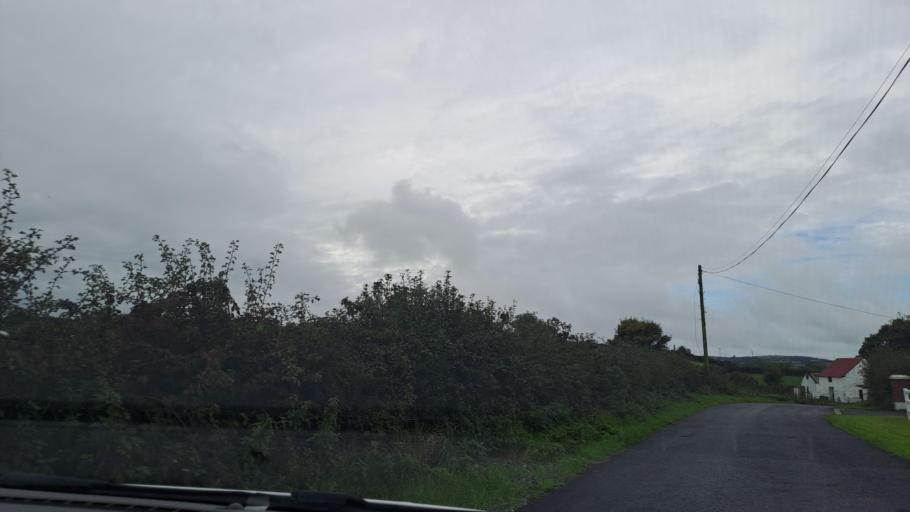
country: IE
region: Ulster
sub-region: An Cabhan
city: Kingscourt
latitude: 53.9810
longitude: -6.8324
